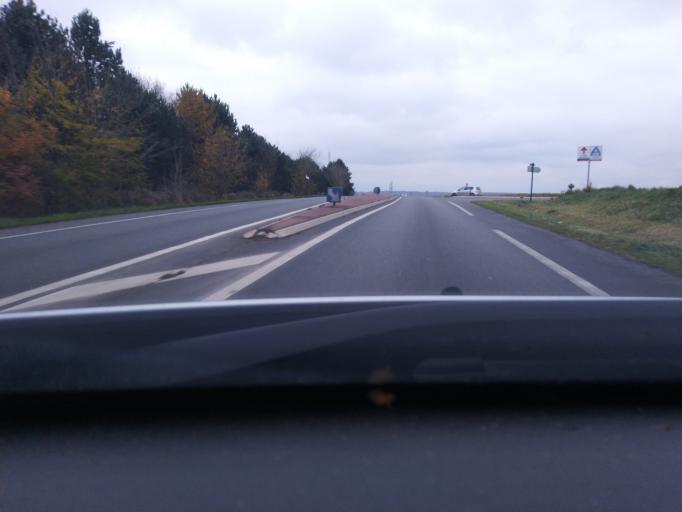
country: FR
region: Nord-Pas-de-Calais
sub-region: Departement du Pas-de-Calais
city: Hesdin
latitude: 50.3517
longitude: 2.0346
